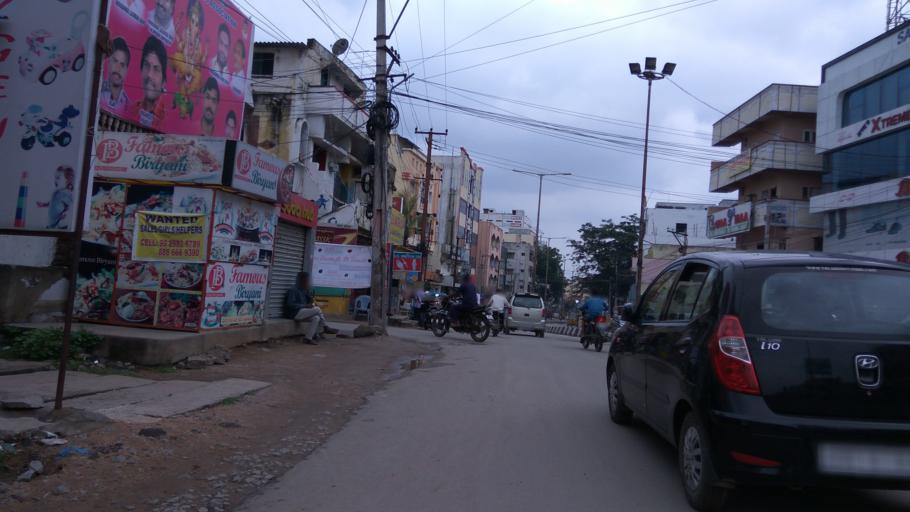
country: IN
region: Telangana
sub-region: Hyderabad
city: Malkajgiri
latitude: 17.4526
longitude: 78.5338
